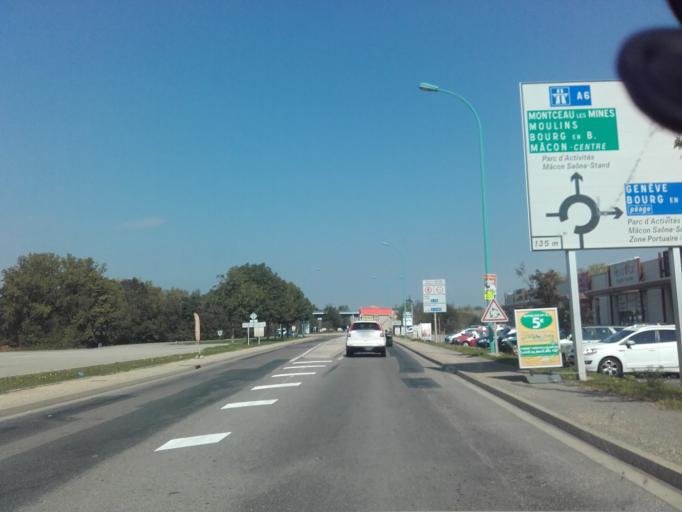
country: FR
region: Bourgogne
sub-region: Departement de Saone-et-Loire
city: Creches-sur-Saone
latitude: 46.2748
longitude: 4.8001
